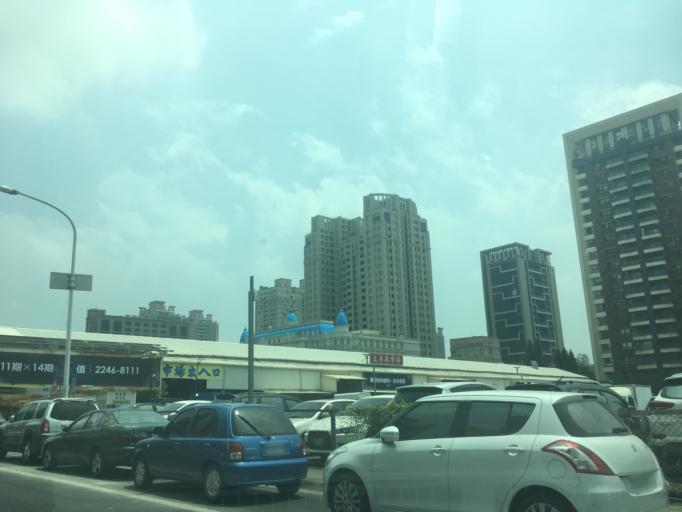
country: TW
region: Taiwan
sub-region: Taichung City
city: Taichung
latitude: 24.1804
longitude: 120.6828
